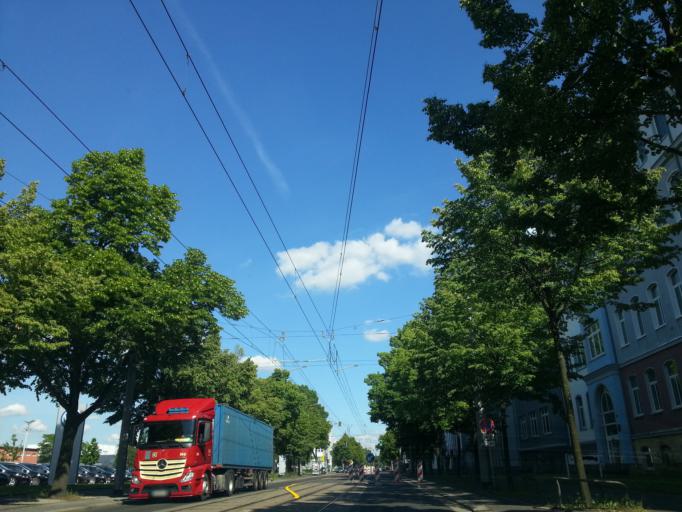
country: DE
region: Saxony
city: Dresden
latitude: 51.0592
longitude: 13.7014
